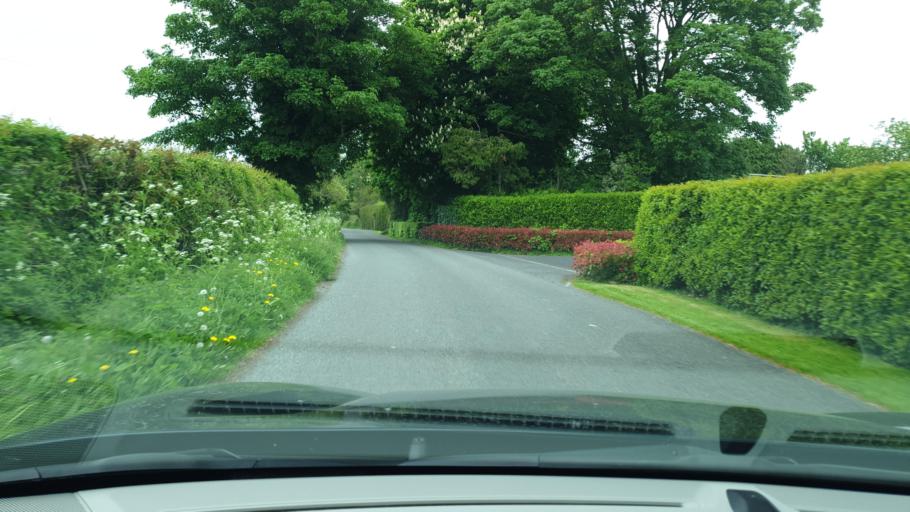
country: IE
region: Leinster
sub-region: An Mhi
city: Dunboyne
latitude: 53.4490
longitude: -6.5071
